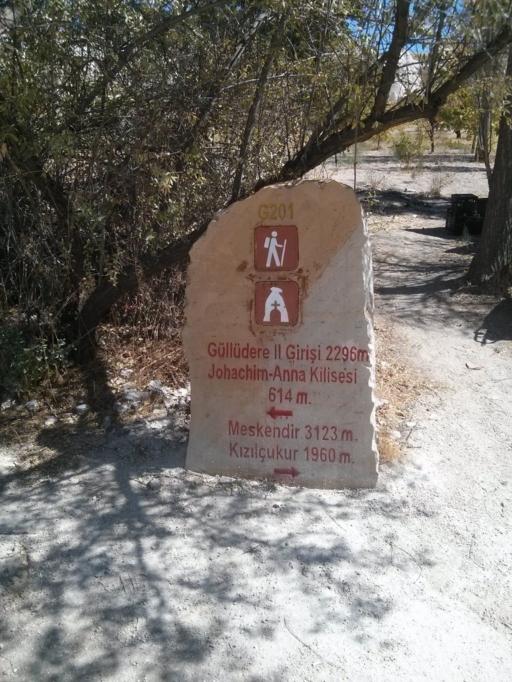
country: TR
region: Nevsehir
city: Goereme
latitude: 38.6557
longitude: 34.8462
